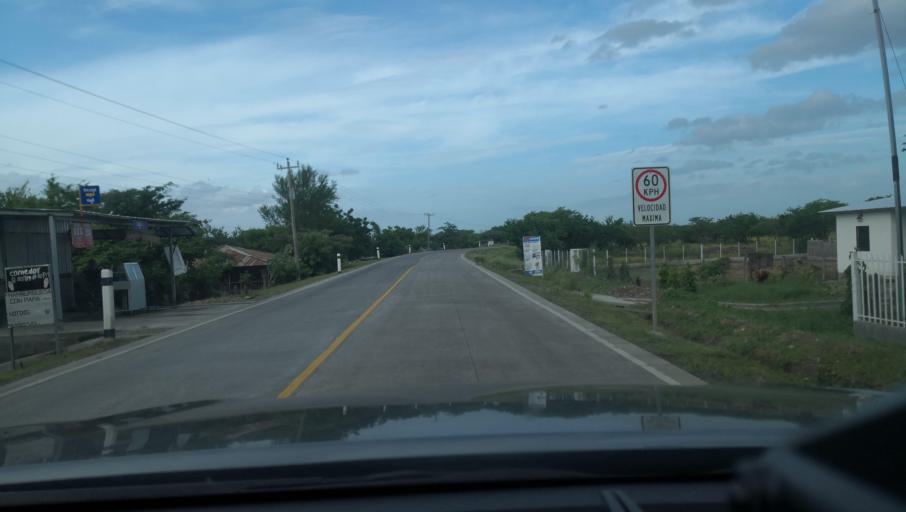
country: NI
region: Boaco
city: San Lorenzo
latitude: 12.2166
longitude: -85.6657
